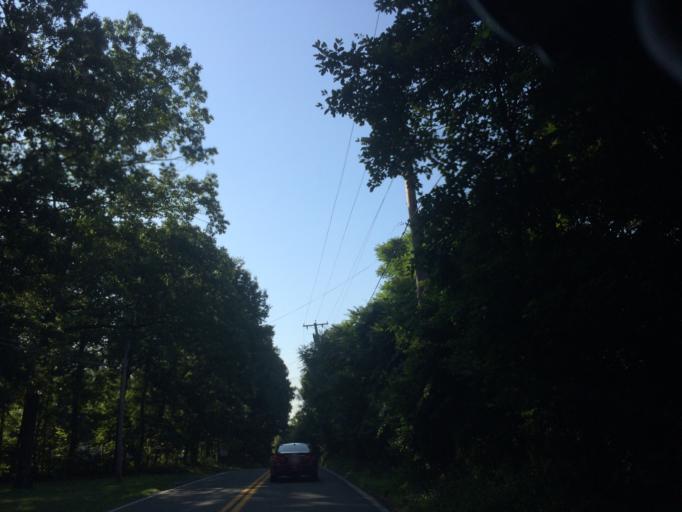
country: US
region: Maryland
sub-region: Montgomery County
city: Olney
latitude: 39.2121
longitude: -77.0435
